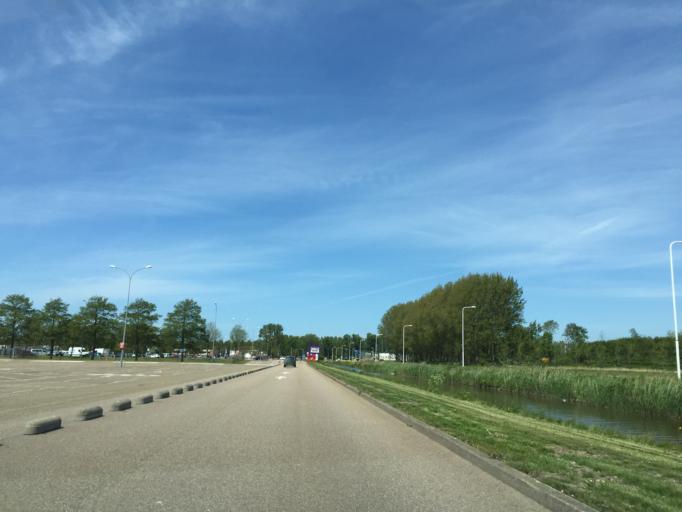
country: NL
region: North Holland
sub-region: Gemeente Beverwijk
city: Beverwijk
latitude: 52.4790
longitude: 4.6785
